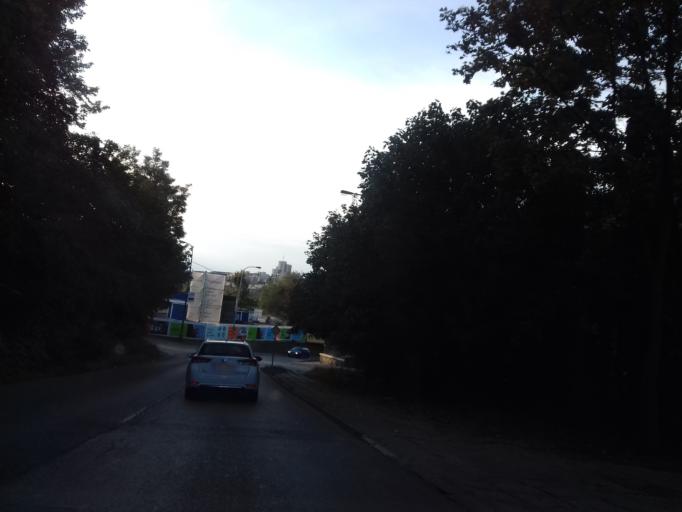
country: CZ
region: Praha
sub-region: Praha 4
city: Hodkovicky
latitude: 50.0319
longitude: 14.4454
